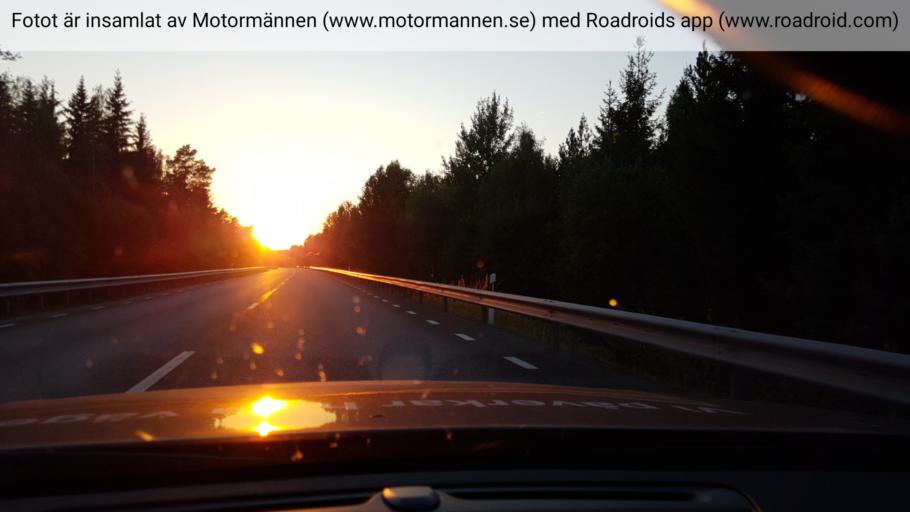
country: SE
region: Uppsala
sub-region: Osthammars Kommun
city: Bjorklinge
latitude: 59.9648
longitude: 17.3856
